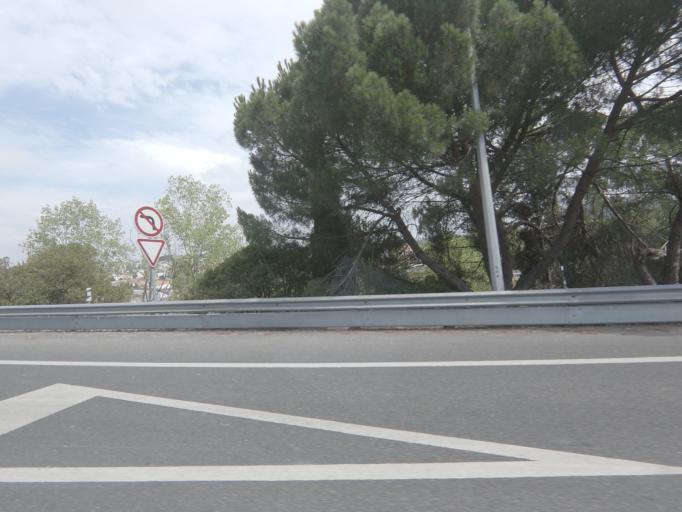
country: PT
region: Leiria
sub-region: Leiria
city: Leiria
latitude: 39.7541
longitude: -8.8161
